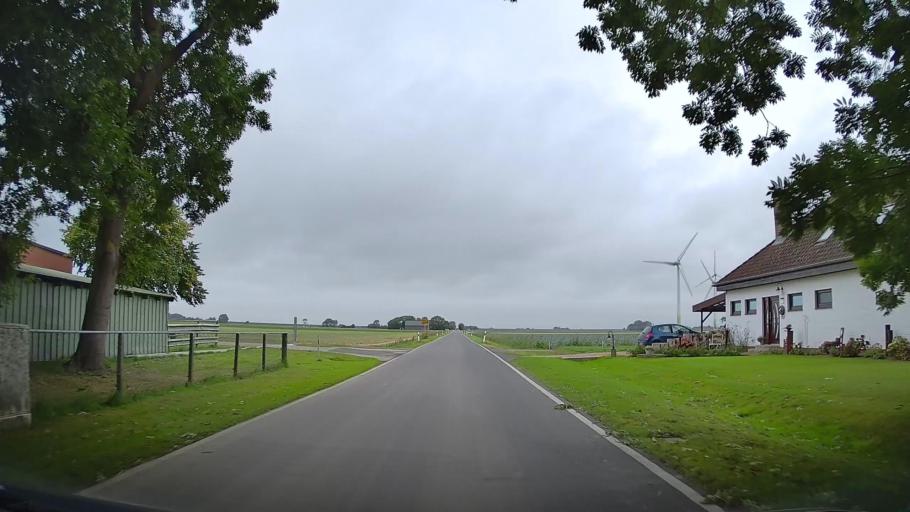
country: DE
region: Schleswig-Holstein
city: Friedrichskoog
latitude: 54.0128
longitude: 8.9029
